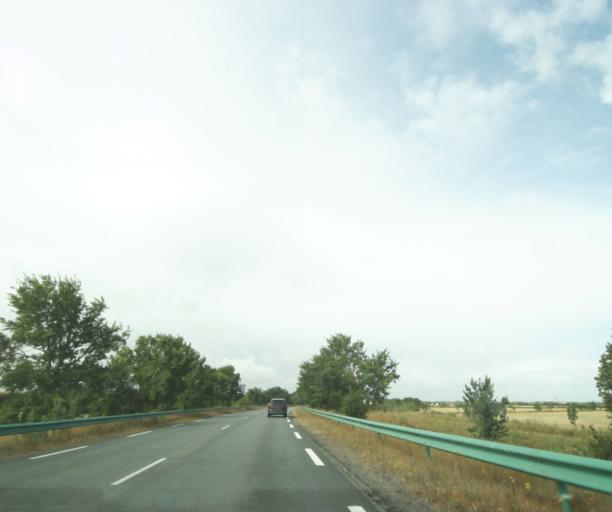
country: FR
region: Poitou-Charentes
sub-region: Departement de la Charente-Maritime
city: Esnandes
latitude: 46.2457
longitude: -1.0714
